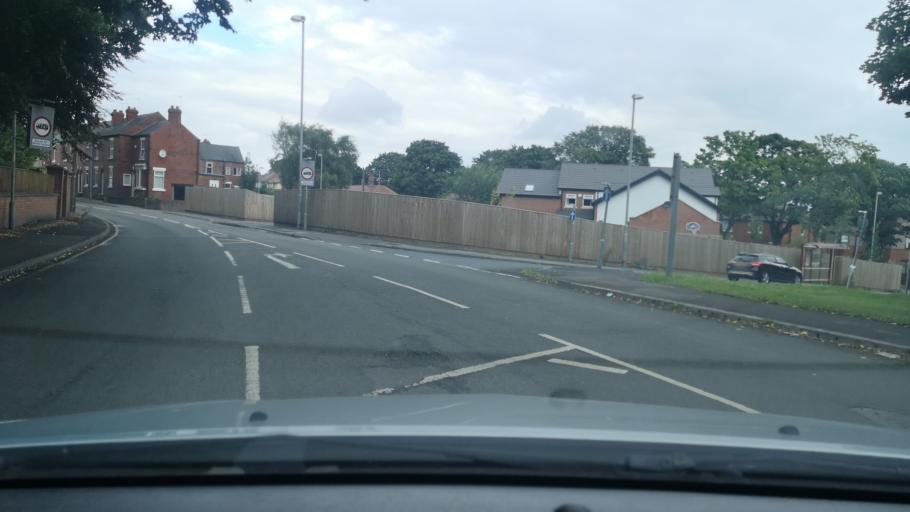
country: GB
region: England
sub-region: City and Borough of Wakefield
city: Wakefield
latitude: 53.6811
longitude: -1.5282
